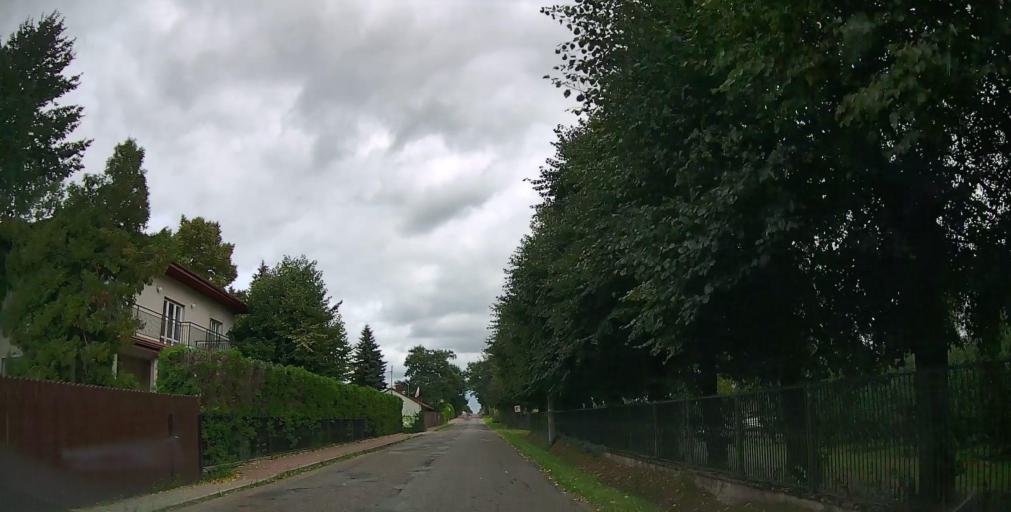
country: PL
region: Masovian Voivodeship
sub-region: Powiat grojecki
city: Belsk Duzy
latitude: 51.8215
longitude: 20.8175
